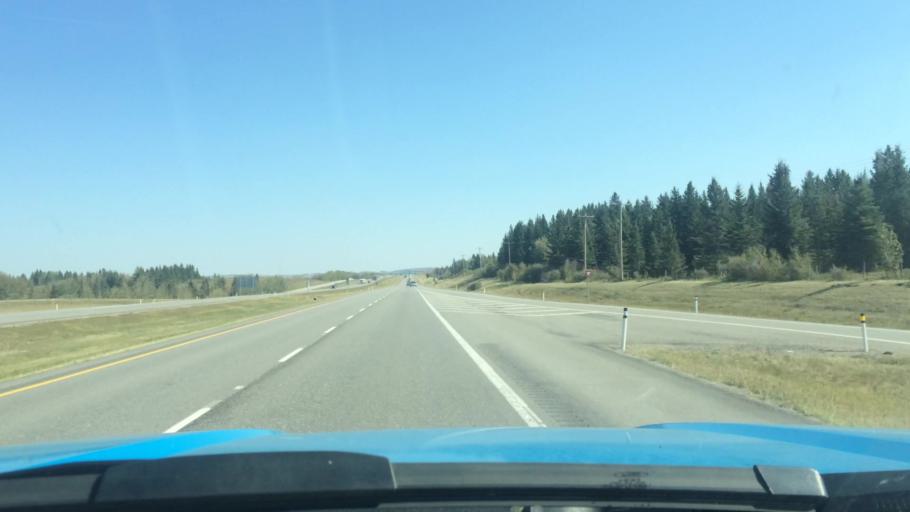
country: CA
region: Alberta
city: Cochrane
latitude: 51.1298
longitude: -114.6913
